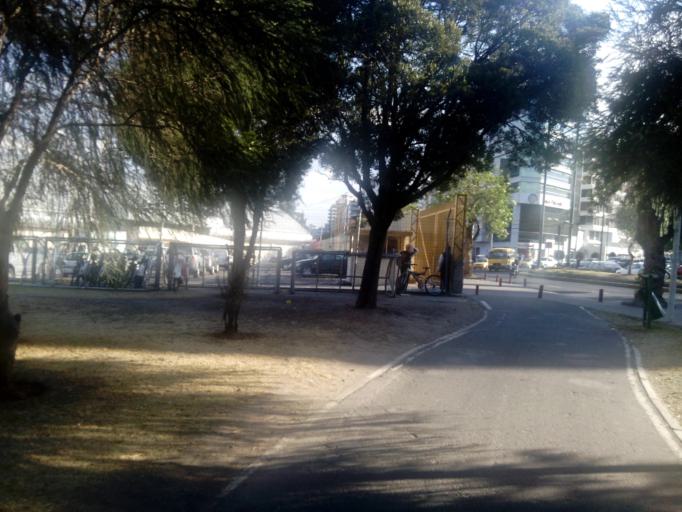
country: EC
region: Pichincha
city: Quito
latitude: -0.1810
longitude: -78.4862
